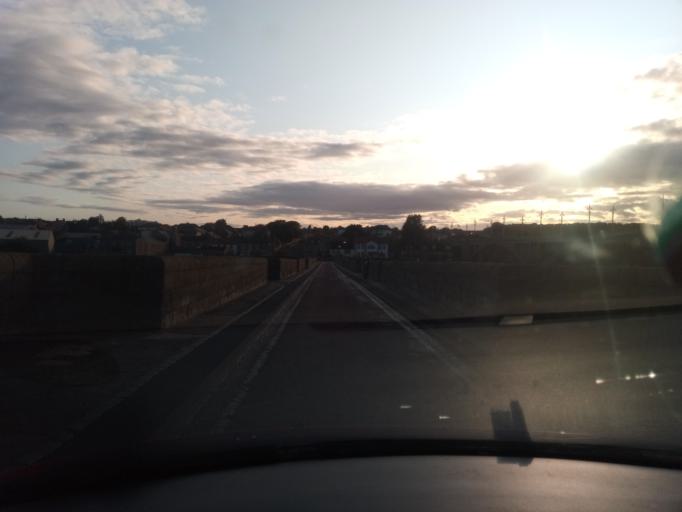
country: GB
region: England
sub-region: Northumberland
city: Berwick-Upon-Tweed
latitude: 55.7680
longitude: -2.0075
